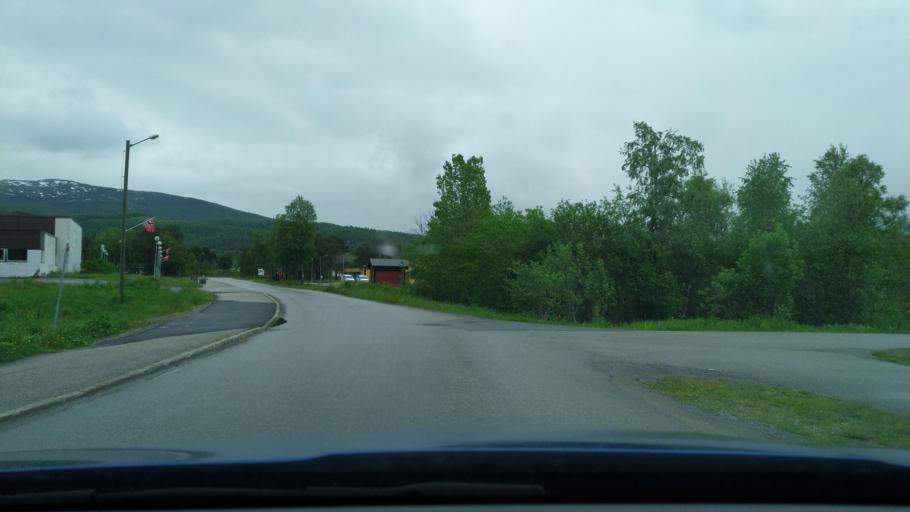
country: NO
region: Troms
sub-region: Dyroy
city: Brostadbotn
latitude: 69.0914
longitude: 17.6959
